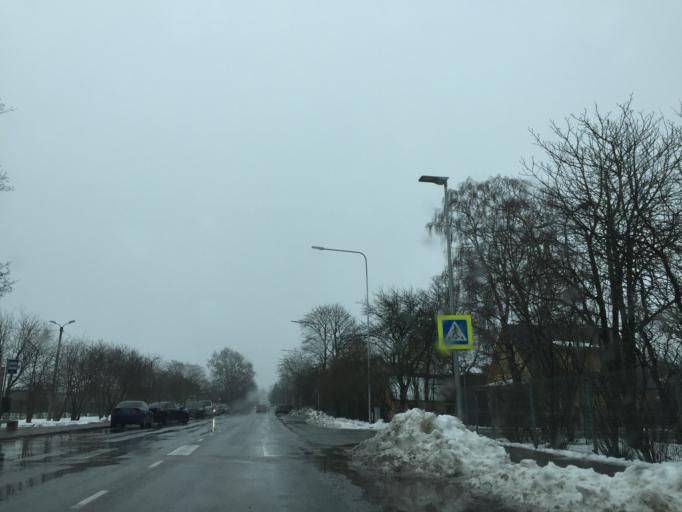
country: EE
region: Saare
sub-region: Kuressaare linn
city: Kuressaare
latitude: 58.2606
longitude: 22.4906
